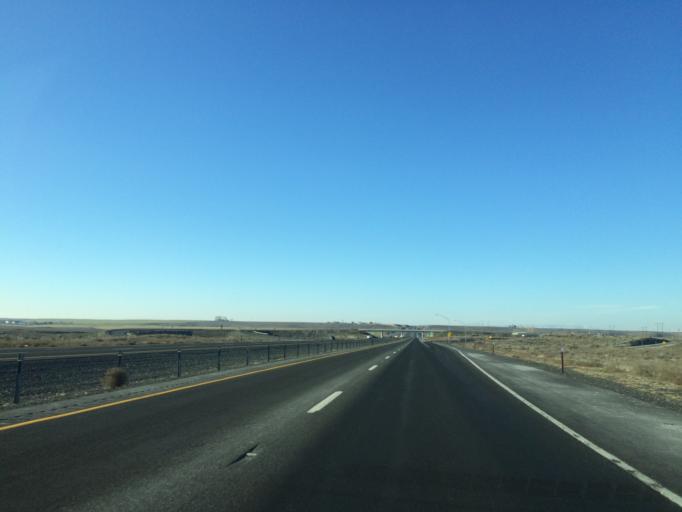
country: US
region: Washington
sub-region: Grant County
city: Cascade Valley
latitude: 47.1042
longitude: -119.4425
